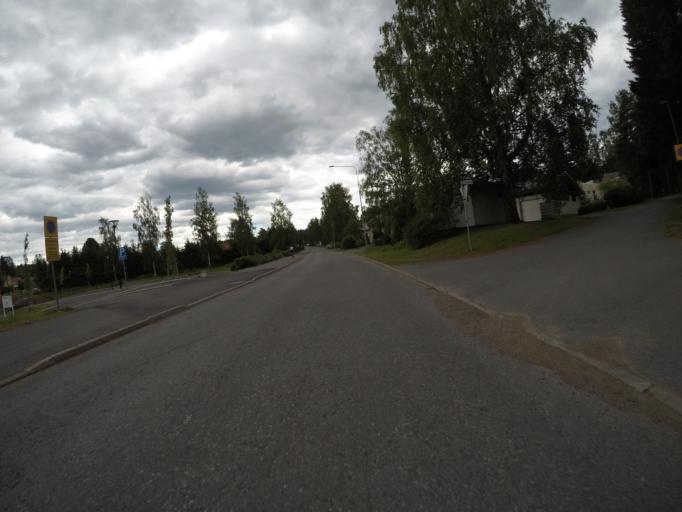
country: FI
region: Haeme
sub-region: Haemeenlinna
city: Haemeenlinna
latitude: 60.9835
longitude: 24.4384
